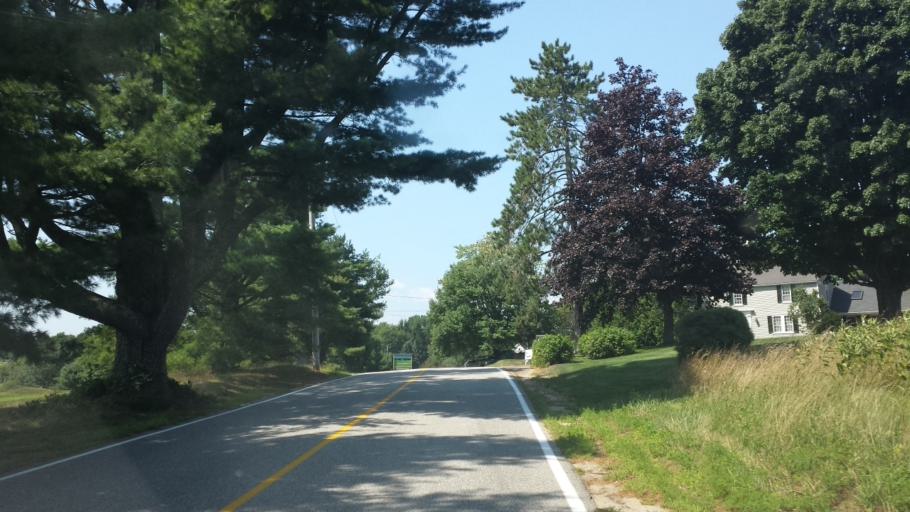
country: US
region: Maine
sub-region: York County
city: Arundel
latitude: 43.3762
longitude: -70.4830
